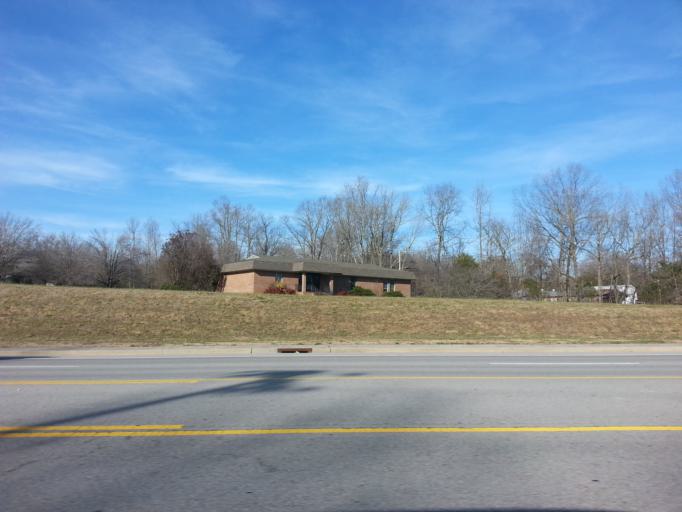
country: US
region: Tennessee
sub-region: Warren County
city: McMinnville
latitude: 35.6978
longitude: -85.8192
